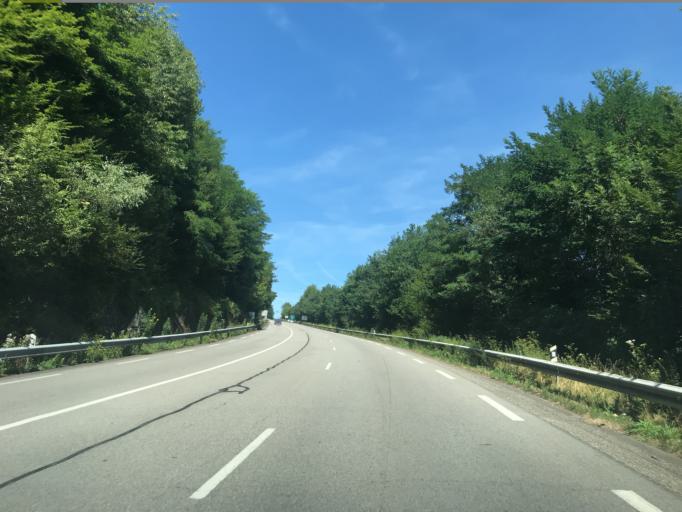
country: FR
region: Limousin
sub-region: Departement de la Correze
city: Tulle
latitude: 45.2667
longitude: 1.7914
